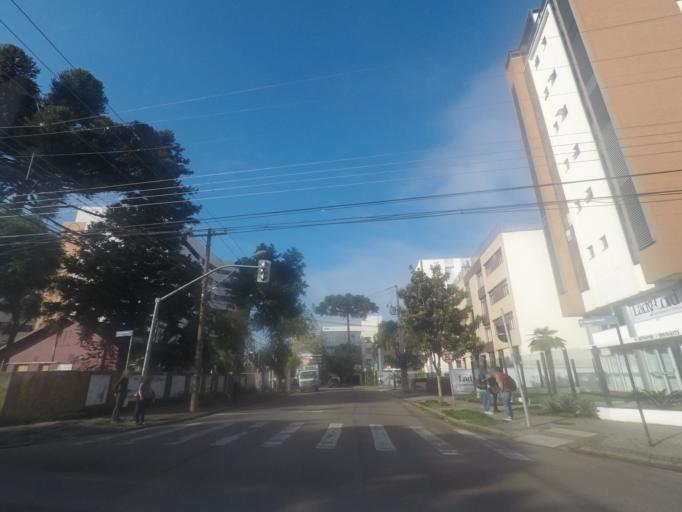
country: BR
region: Parana
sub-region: Curitiba
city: Curitiba
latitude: -25.4094
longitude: -49.2644
